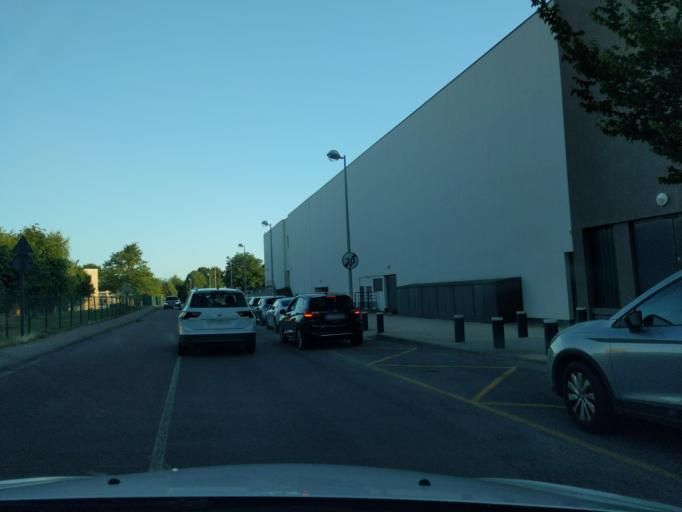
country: FR
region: Bourgogne
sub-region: Departement de la Cote-d'Or
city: Saint-Apollinaire
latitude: 47.3127
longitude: 5.0921
